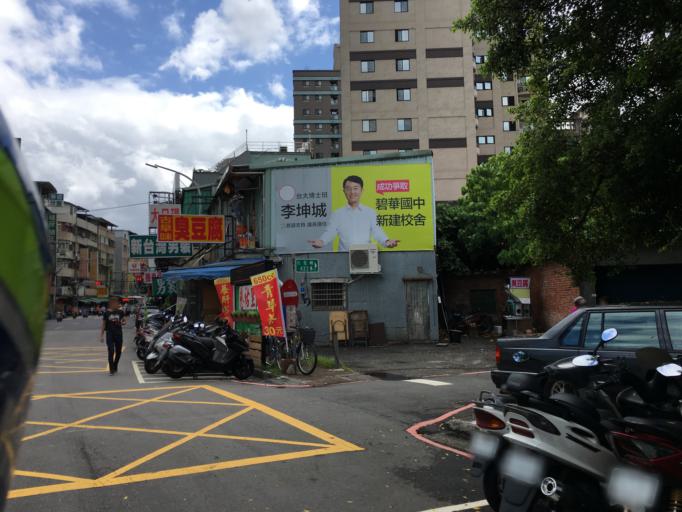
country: TW
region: Taipei
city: Taipei
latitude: 25.0815
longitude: 121.4903
